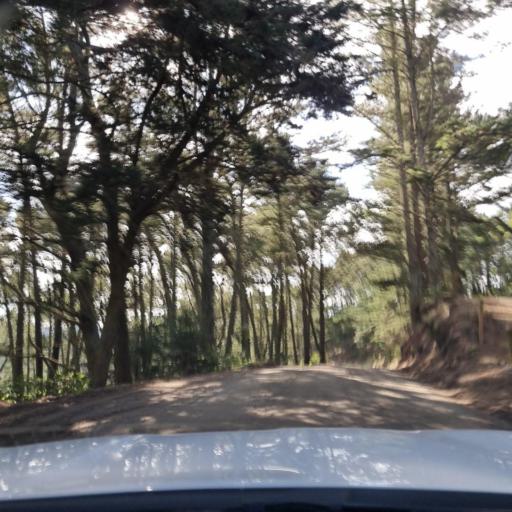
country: NZ
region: Auckland
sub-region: Auckland
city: Wellsford
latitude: -36.3131
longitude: 174.1292
